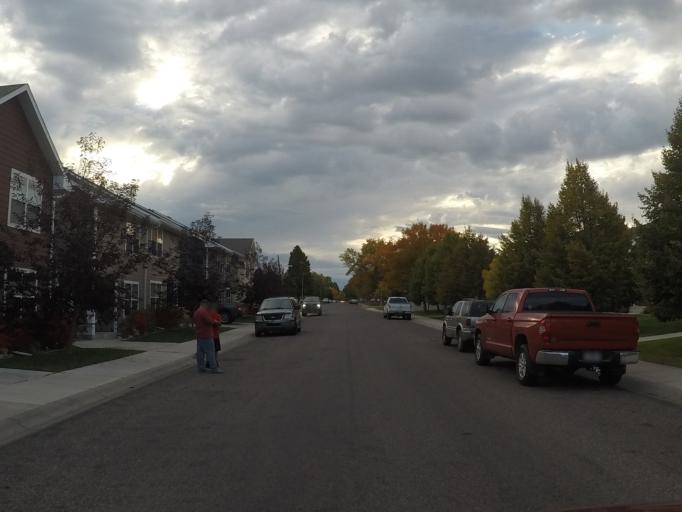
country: US
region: Montana
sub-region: Yellowstone County
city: Billings
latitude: 45.7880
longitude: -108.5373
